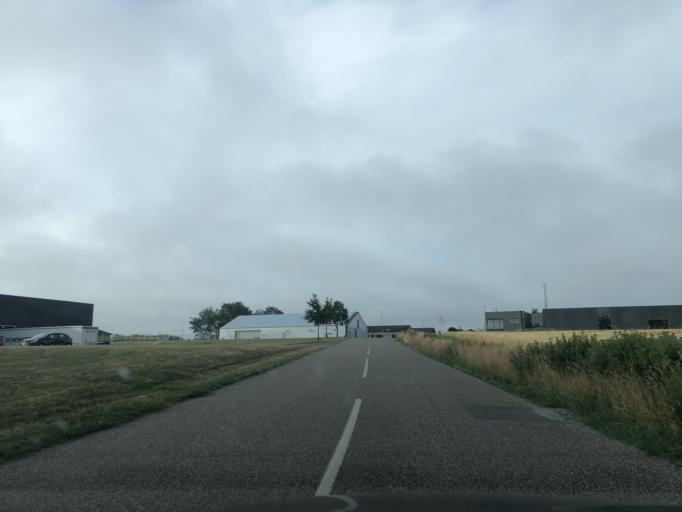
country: DK
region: Central Jutland
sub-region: Silkeborg Kommune
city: Svejbaek
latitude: 56.1592
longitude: 9.6469
